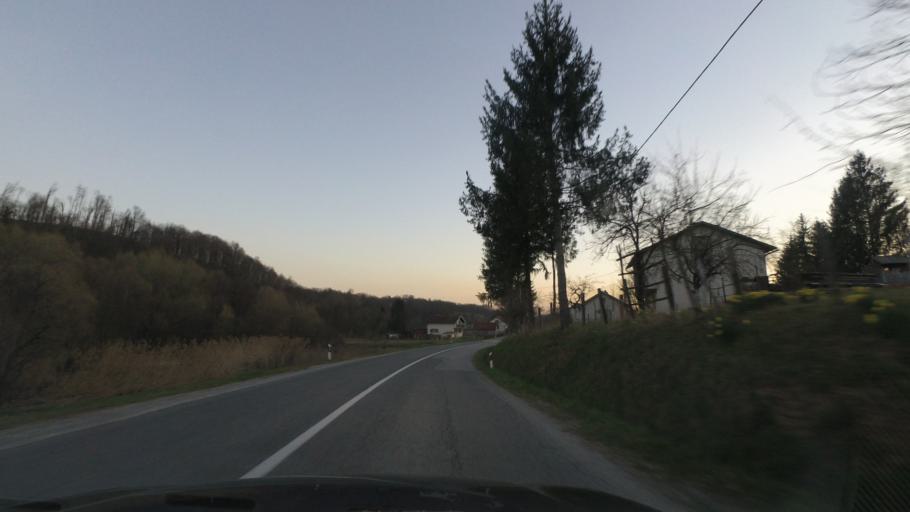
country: HR
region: Karlovacka
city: Vojnic
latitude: 45.3305
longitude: 15.7133
